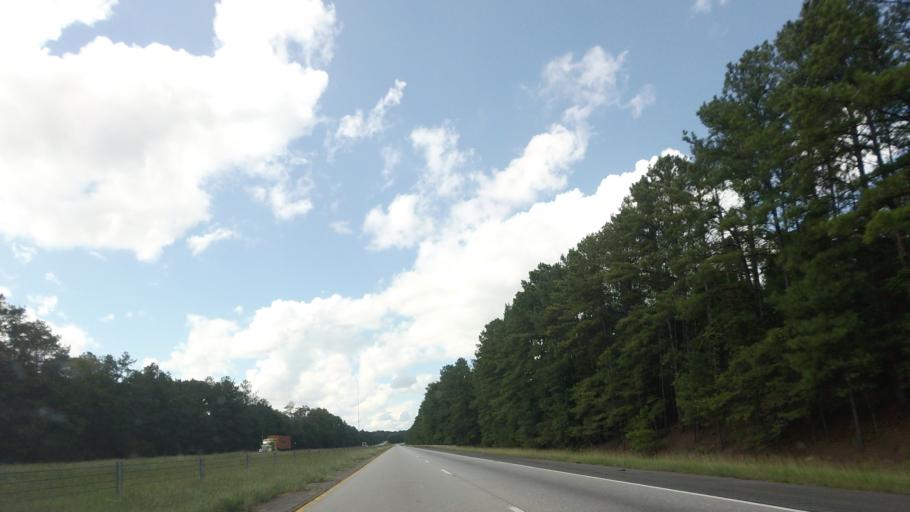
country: US
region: Georgia
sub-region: Bibb County
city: Macon
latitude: 32.7528
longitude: -83.5504
